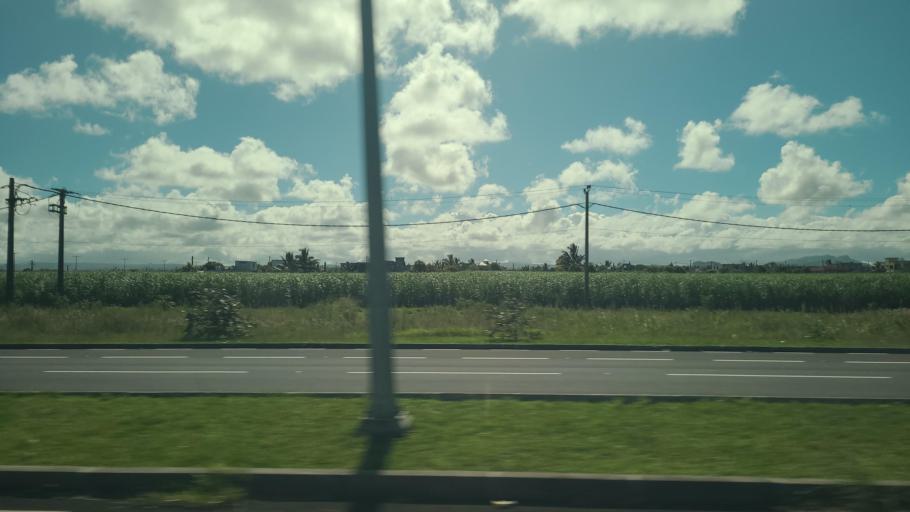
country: MU
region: Grand Port
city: Plaine Magnien
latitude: -20.4411
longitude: 57.6691
